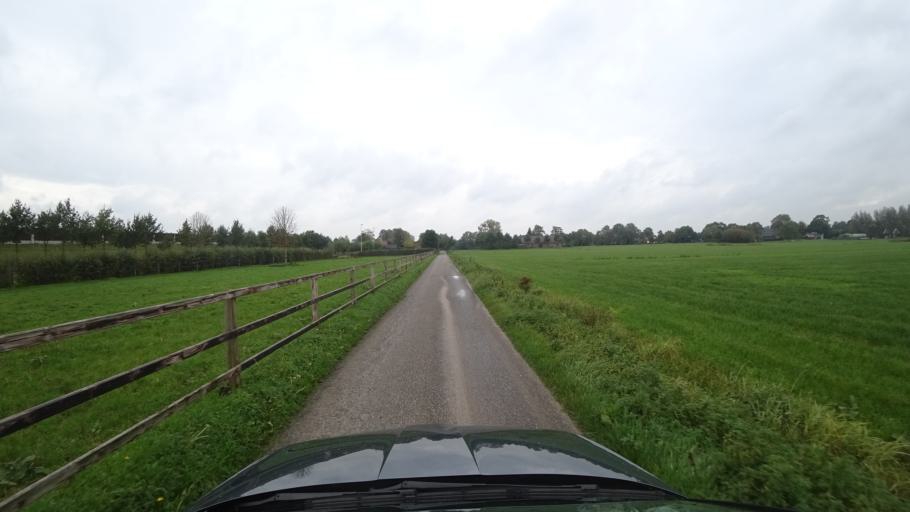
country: NL
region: Gelderland
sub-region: Gemeente Ede
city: Lunteren
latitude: 52.0741
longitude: 5.6041
